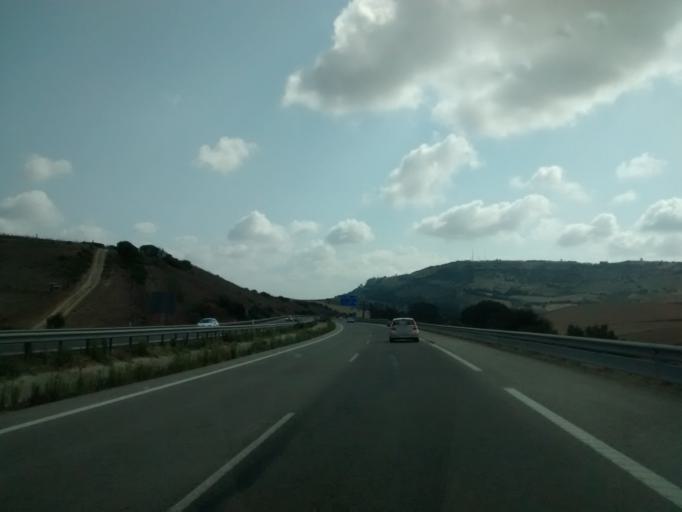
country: ES
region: Andalusia
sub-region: Provincia de Cadiz
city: Vejer de la Frontera
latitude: 36.2527
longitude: -5.9957
